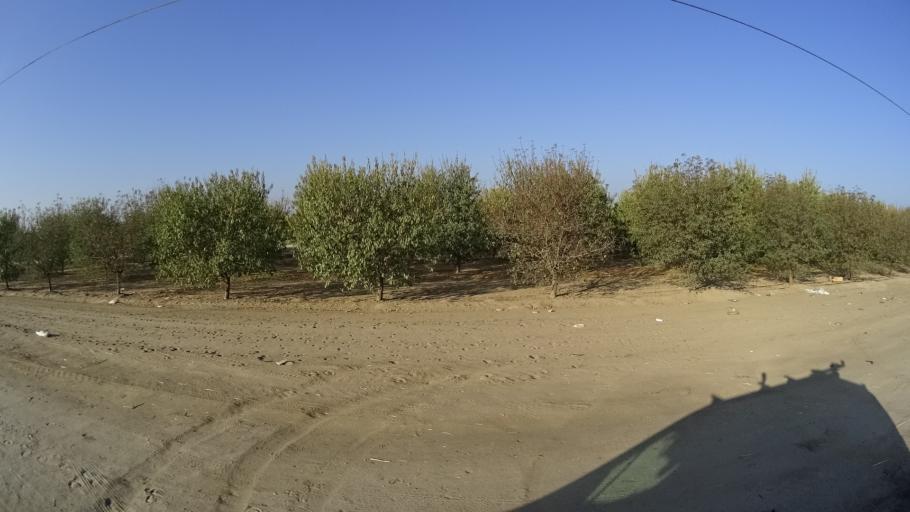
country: US
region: California
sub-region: Kern County
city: Greenfield
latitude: 35.2654
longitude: -118.9854
